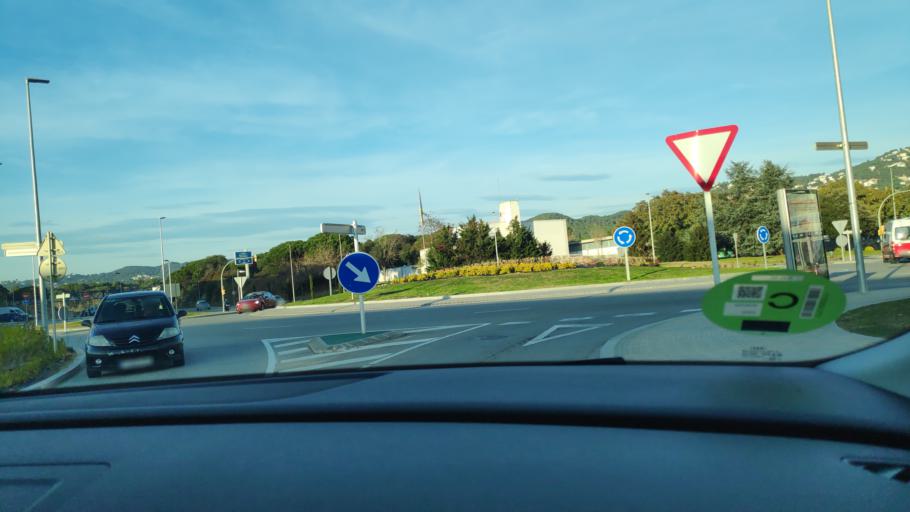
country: ES
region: Catalonia
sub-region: Provincia de Girona
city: Lloret de Mar
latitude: 41.7040
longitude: 2.8357
